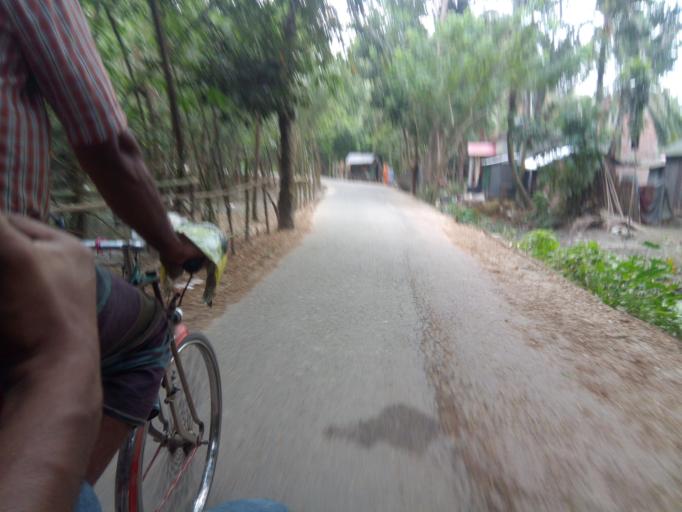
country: BD
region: Khulna
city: Kalia
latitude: 23.2164
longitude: 89.7040
